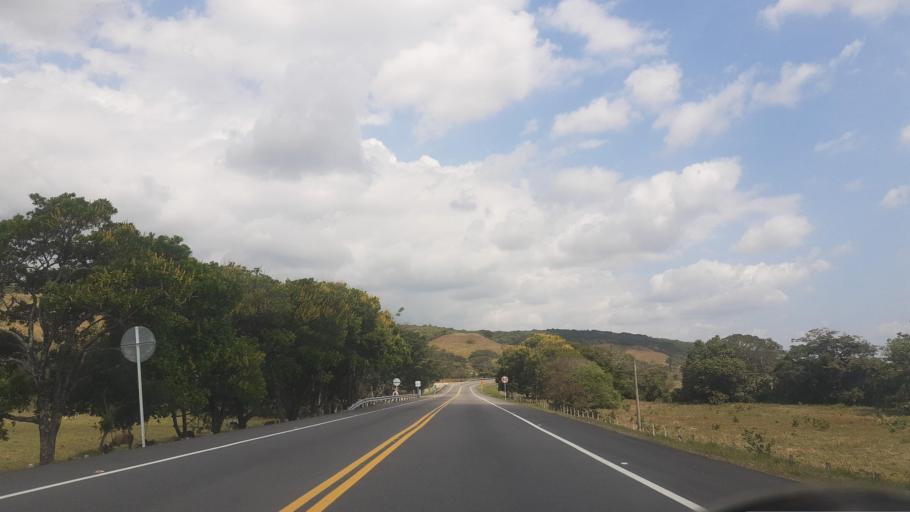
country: CO
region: Casanare
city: Tauramena
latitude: 4.8712
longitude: -72.7049
